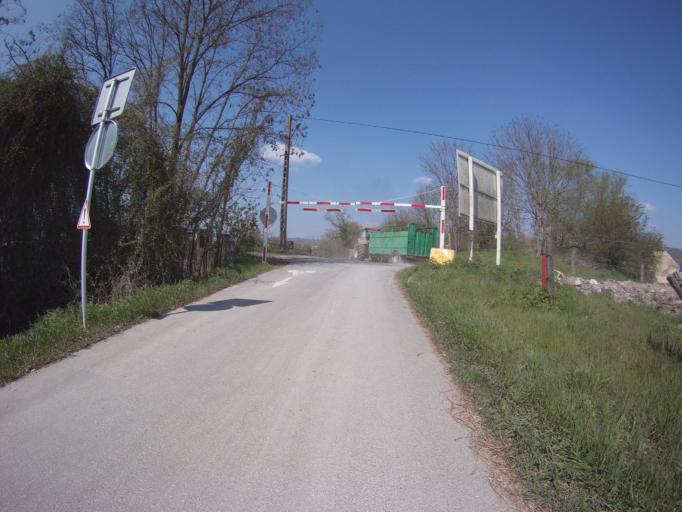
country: FR
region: Lorraine
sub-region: Departement de Meurthe-et-Moselle
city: Blenod-les-Pont-a-Mousson
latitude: 48.8837
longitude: 6.0619
